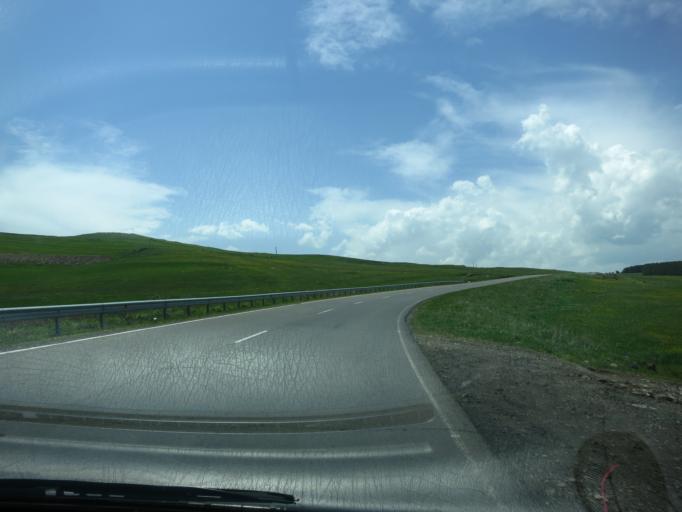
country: GE
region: Samtskhe-Javakheti
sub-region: Ninotsminda
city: Ninotsminda
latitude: 41.2939
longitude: 43.7468
